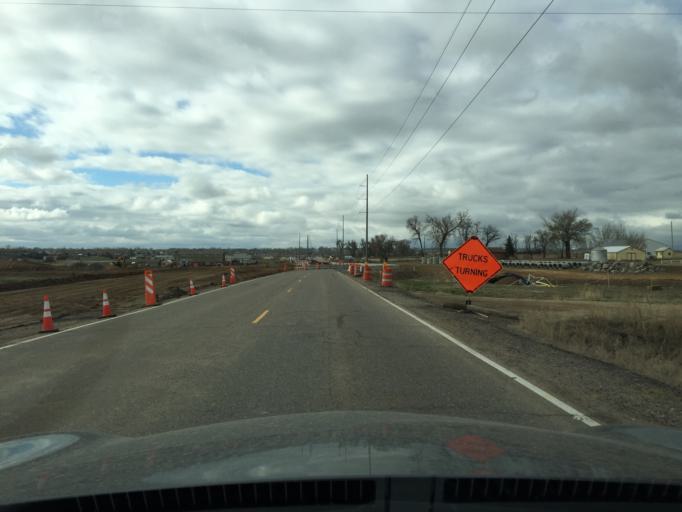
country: US
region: Colorado
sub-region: Adams County
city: Northglenn
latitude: 39.9633
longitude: -104.9784
